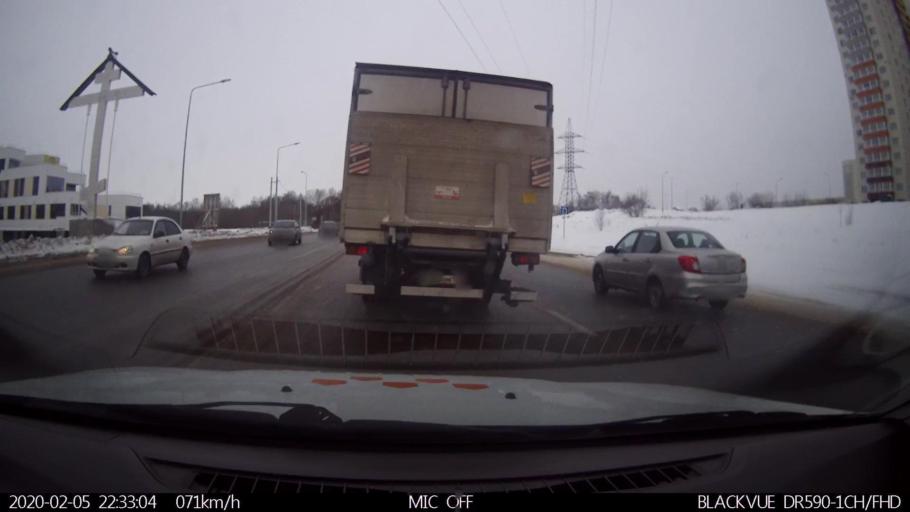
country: RU
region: Nizjnij Novgorod
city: Imeni Stepana Razina
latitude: 54.7370
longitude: 44.2021
